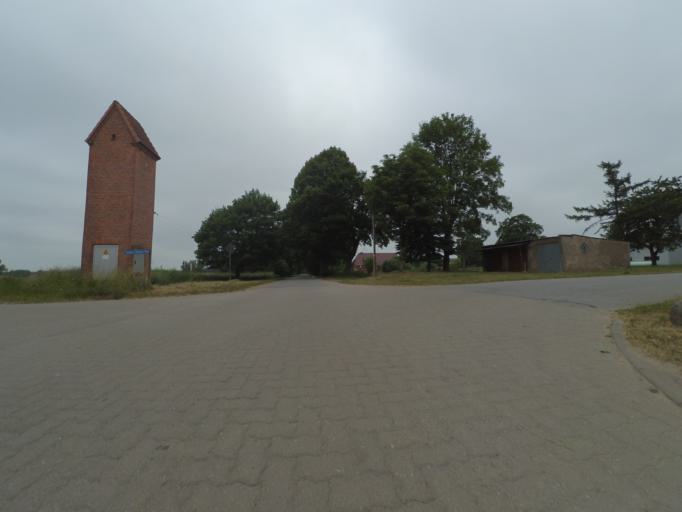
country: DE
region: Mecklenburg-Vorpommern
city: Goldberg
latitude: 53.5253
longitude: 12.1623
